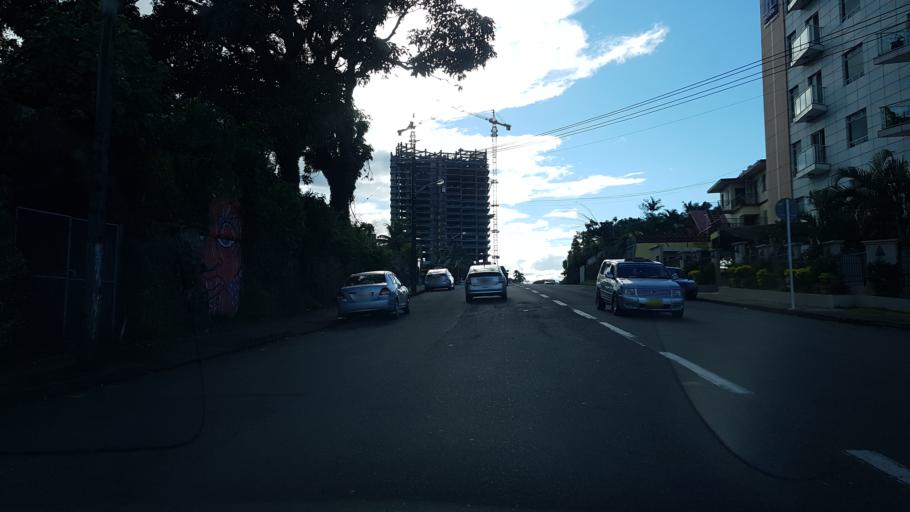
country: FJ
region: Central
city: Suva
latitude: -18.1453
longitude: 178.4275
